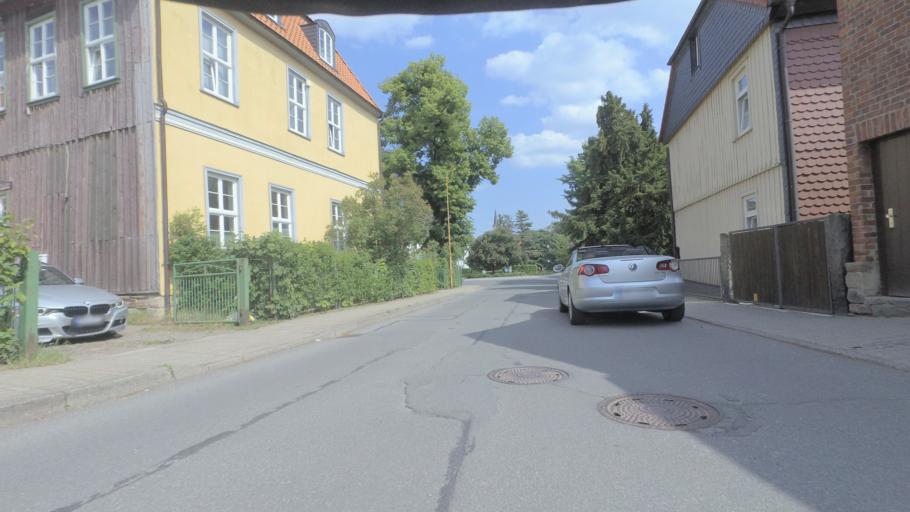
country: DE
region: Saxony-Anhalt
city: Ilsenburg
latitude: 51.8666
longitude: 10.6742
